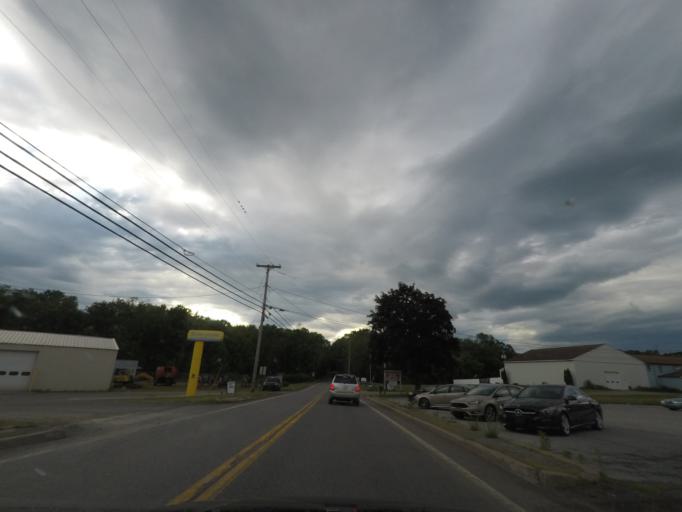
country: US
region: New York
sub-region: Dutchess County
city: Pine Plains
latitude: 41.9832
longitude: -73.6664
